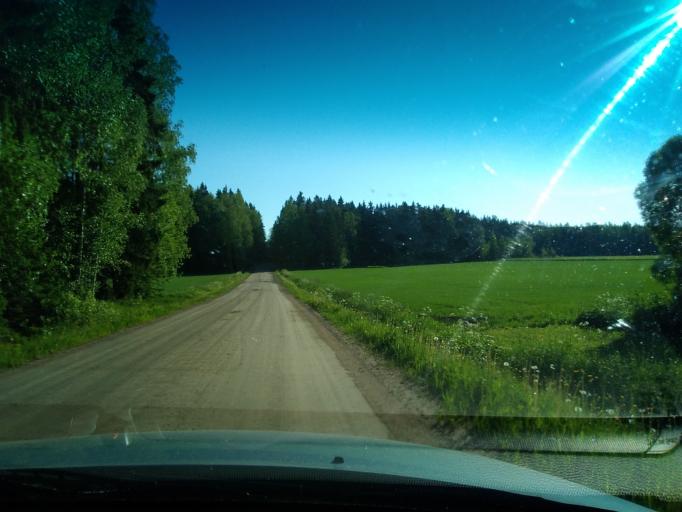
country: FI
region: Haeme
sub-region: Forssa
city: Tammela
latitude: 60.7620
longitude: 23.7995
